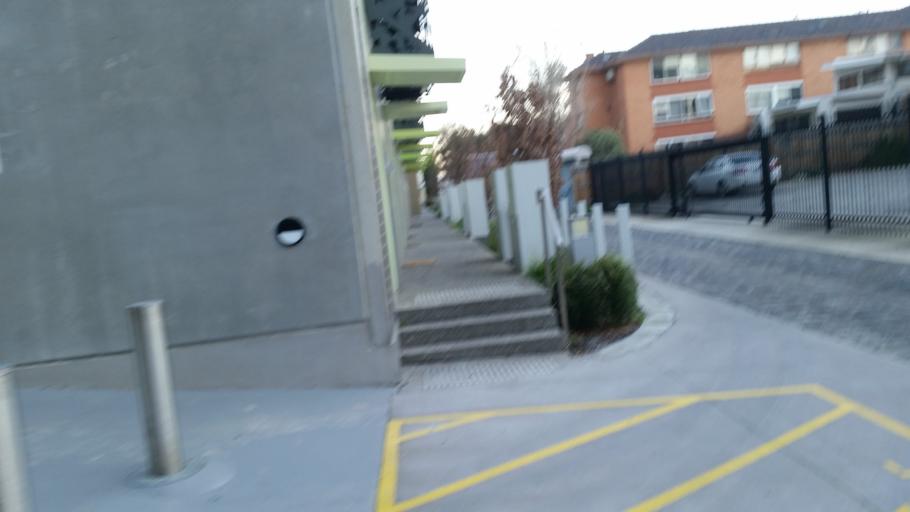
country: AU
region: Victoria
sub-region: Yarra
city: Richmond
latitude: -37.8123
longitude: 145.0090
